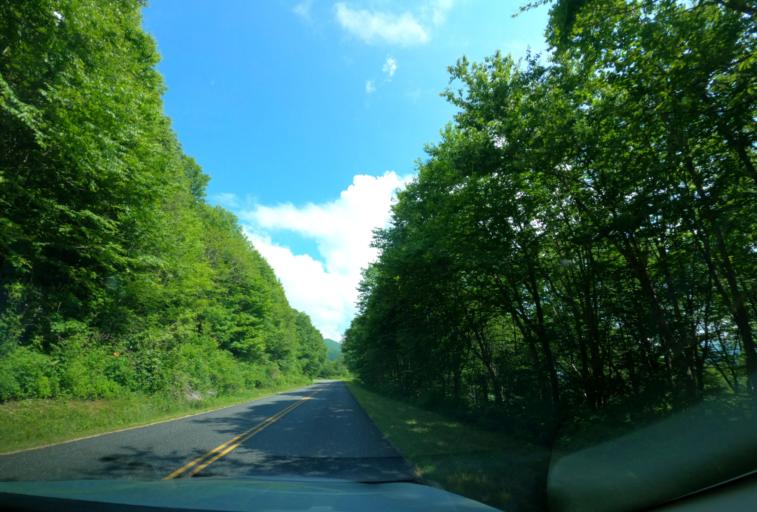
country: US
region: North Carolina
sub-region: Haywood County
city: Hazelwood
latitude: 35.3937
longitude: -83.0380
